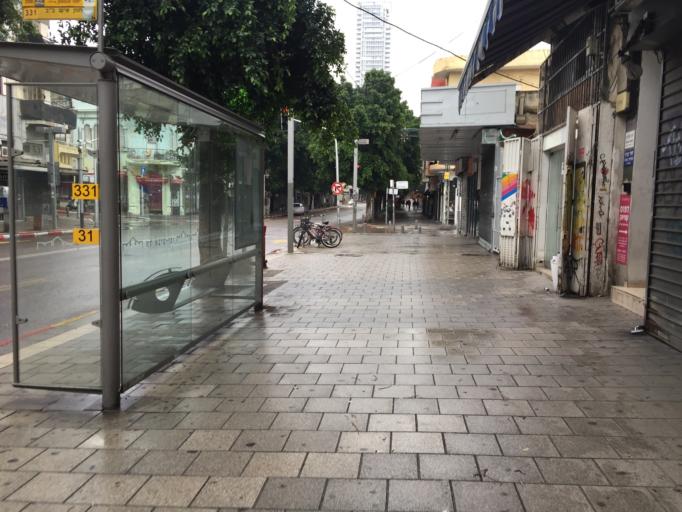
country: IL
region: Tel Aviv
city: Tel Aviv
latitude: 32.0674
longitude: 34.7712
